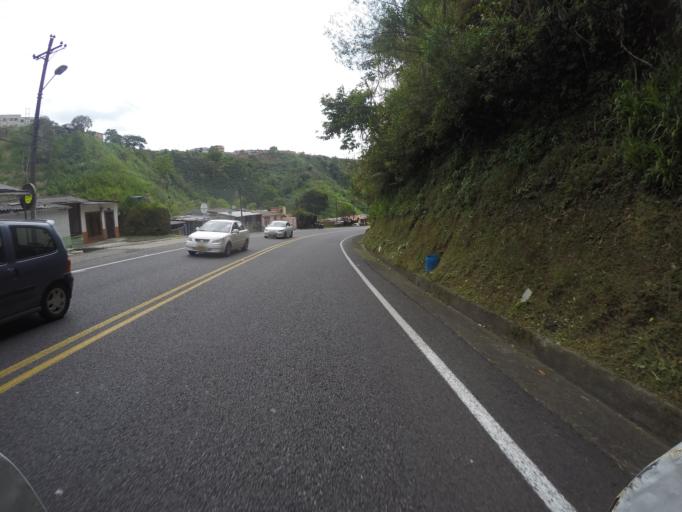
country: CO
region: Risaralda
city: Pereira
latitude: 4.7839
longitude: -75.6964
